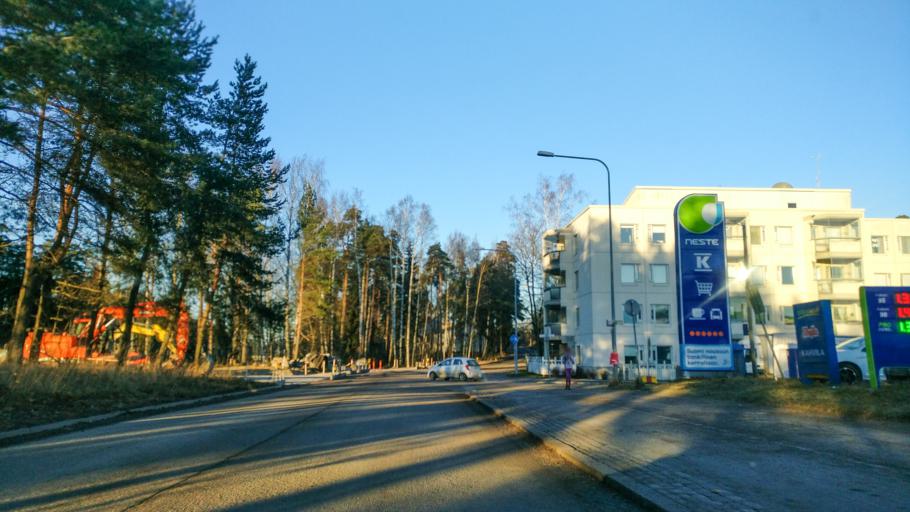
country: FI
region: Uusimaa
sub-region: Helsinki
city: Vantaa
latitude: 60.1804
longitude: 25.0511
